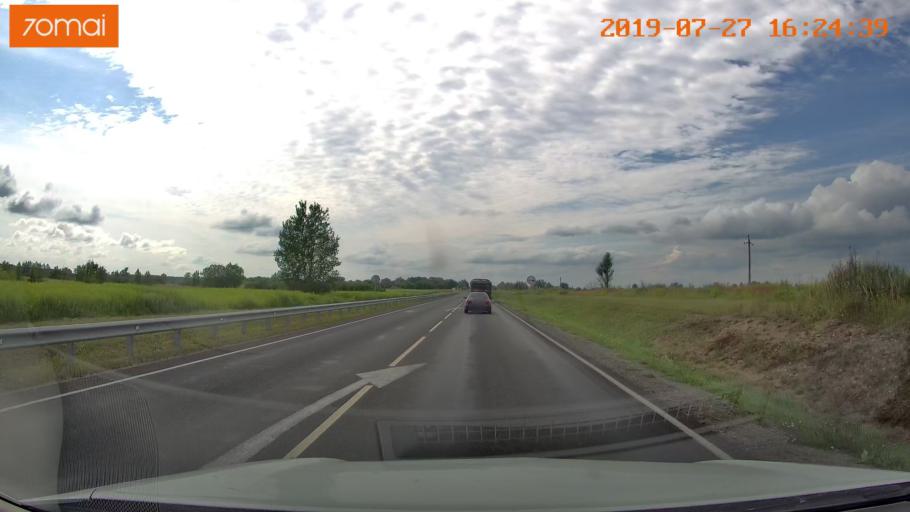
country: RU
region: Kaliningrad
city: Zheleznodorozhnyy
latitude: 54.6348
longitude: 21.4478
